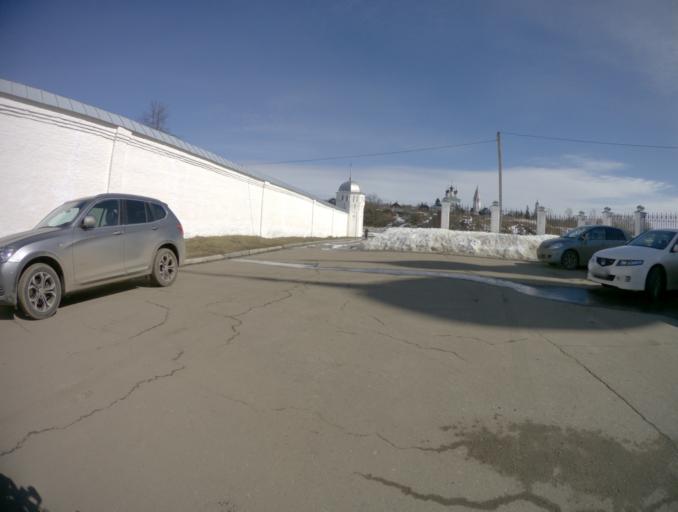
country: RU
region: Vladimir
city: Suzdal'
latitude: 56.4282
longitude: 40.4364
